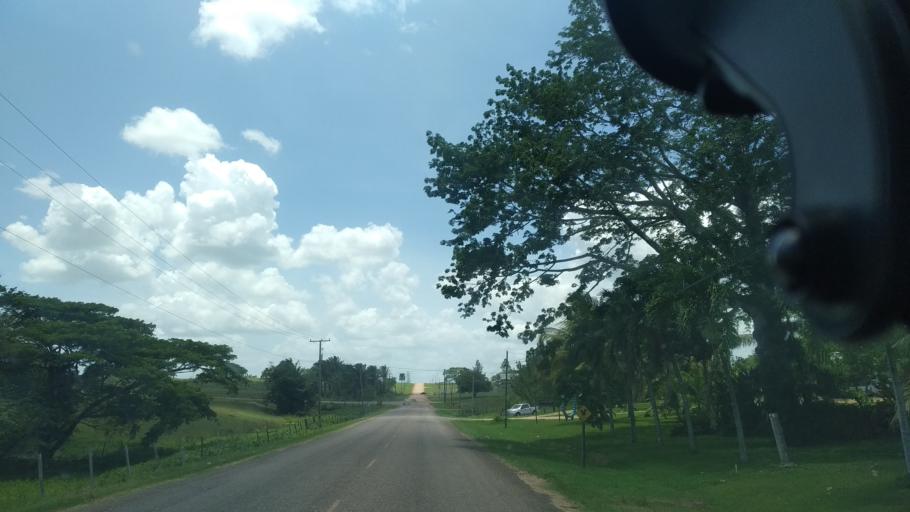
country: BZ
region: Cayo
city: San Ignacio
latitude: 17.2542
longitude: -88.9874
